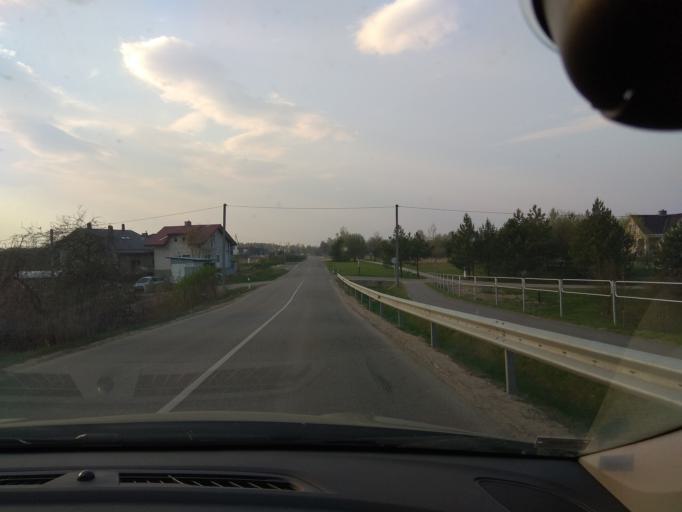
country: LT
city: Grigiskes
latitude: 54.6204
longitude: 25.1142
